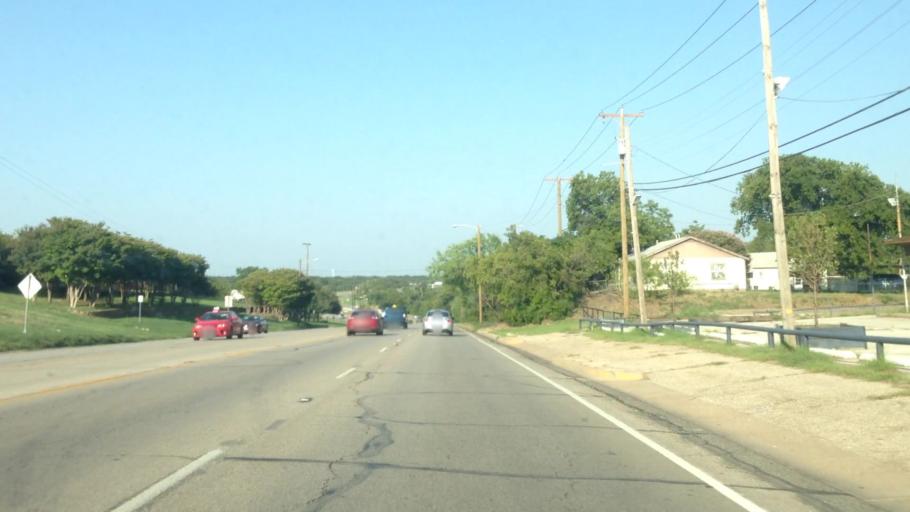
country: US
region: Texas
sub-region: Tarrant County
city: Haltom City
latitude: 32.8053
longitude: -97.2543
